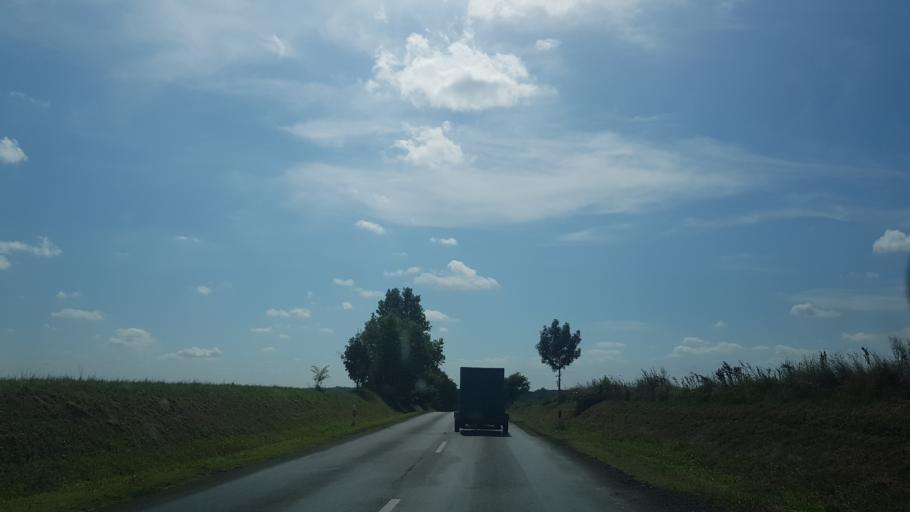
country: HU
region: Somogy
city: Bohonye
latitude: 46.4695
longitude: 17.3834
